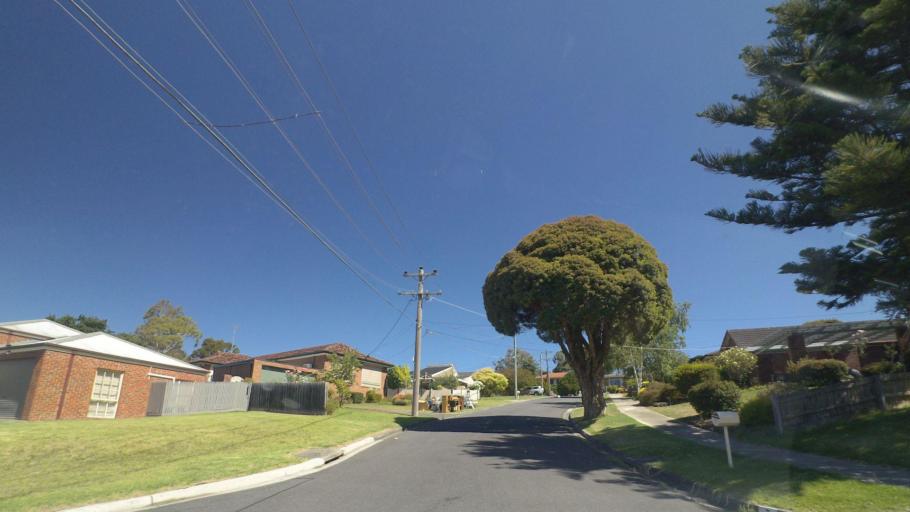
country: AU
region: Victoria
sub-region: Yarra Ranges
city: Chirnside Park
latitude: -37.7471
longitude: 145.3261
